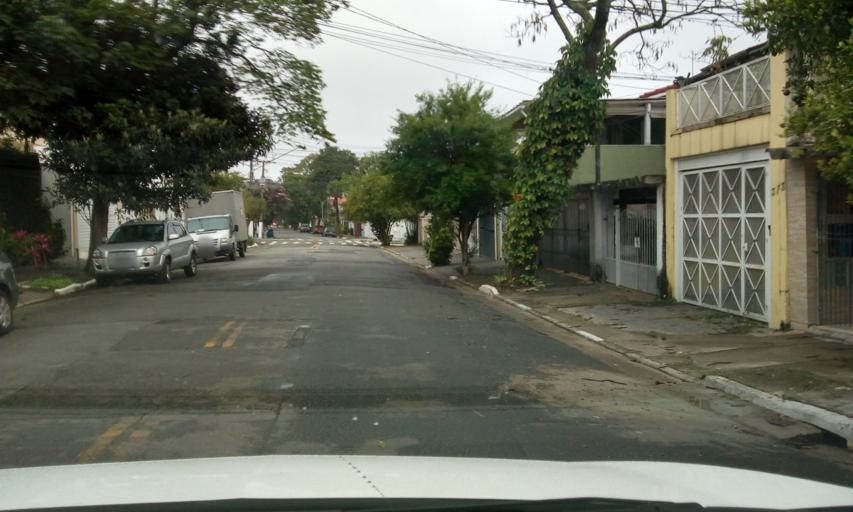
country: BR
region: Sao Paulo
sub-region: Sao Paulo
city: Sao Paulo
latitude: -23.6088
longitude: -46.6473
